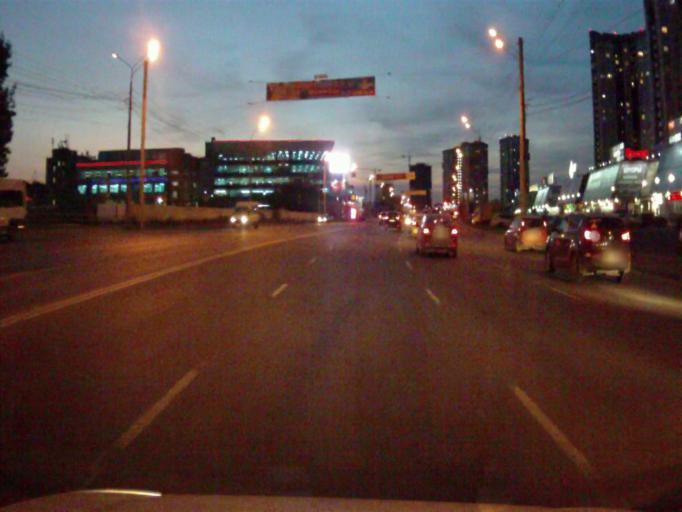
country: RU
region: Chelyabinsk
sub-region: Gorod Chelyabinsk
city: Chelyabinsk
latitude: 55.1679
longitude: 61.3797
